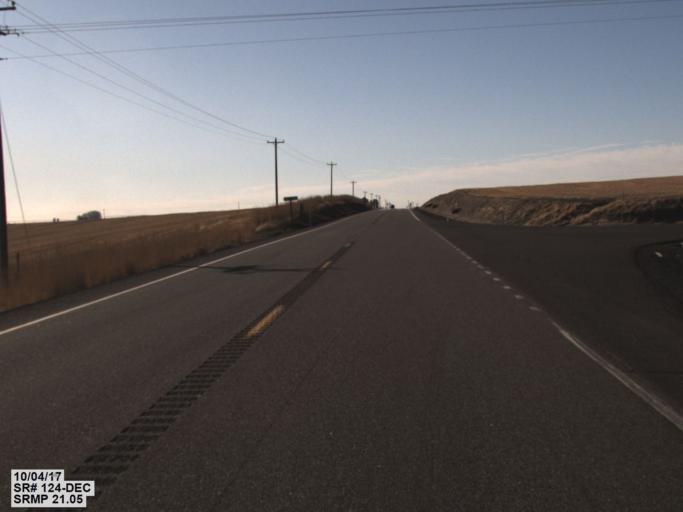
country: US
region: Washington
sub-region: Walla Walla County
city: Garrett
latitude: 46.2962
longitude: -118.6163
